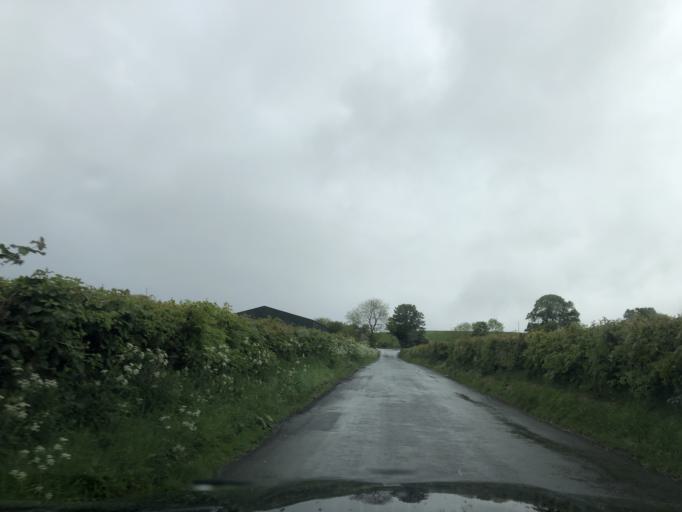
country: GB
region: Northern Ireland
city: Dunloy
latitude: 55.1302
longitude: -6.3733
